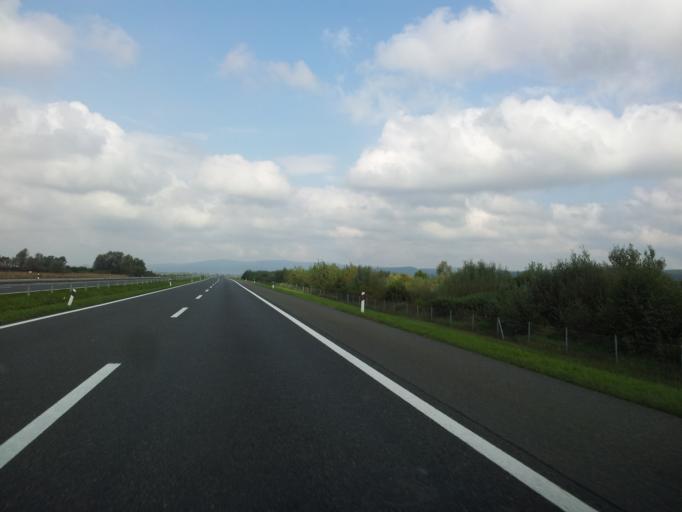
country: HR
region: Brodsko-Posavska
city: Okucani
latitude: 45.2523
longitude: 17.1764
